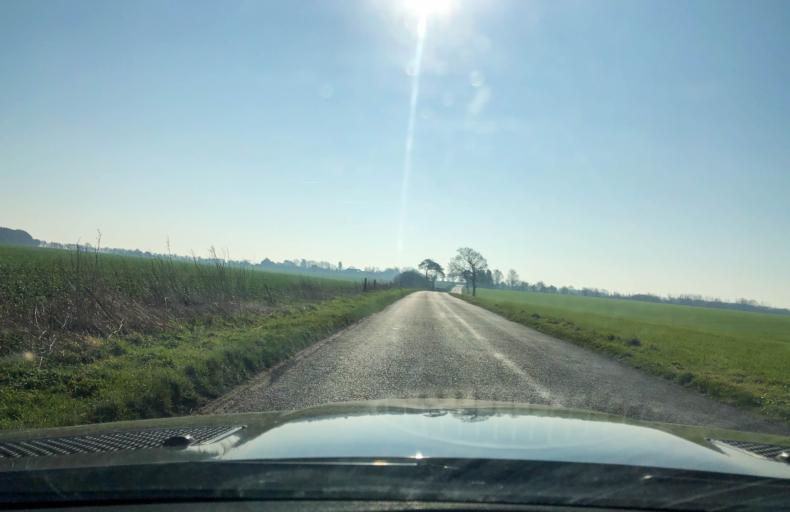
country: GB
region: England
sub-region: Warwickshire
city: Wellesbourne Mountford
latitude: 52.1734
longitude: -1.5257
